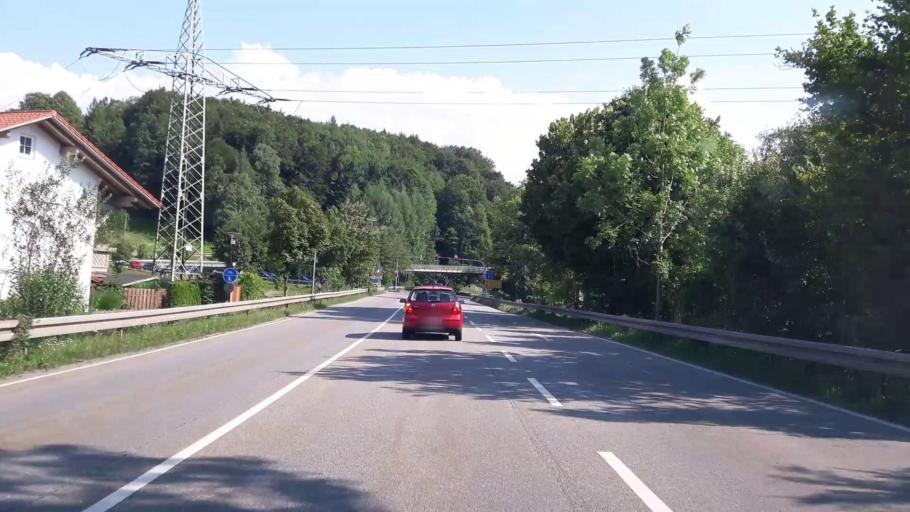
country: DE
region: Bavaria
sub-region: Upper Bavaria
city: Traunstein
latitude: 47.8574
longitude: 12.6378
